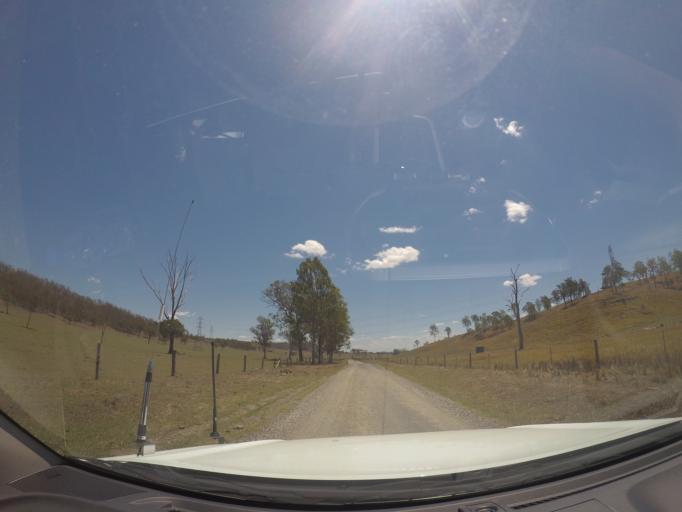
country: AU
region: Queensland
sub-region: Ipswich
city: Redbank Plains
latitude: -27.7523
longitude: 152.8336
